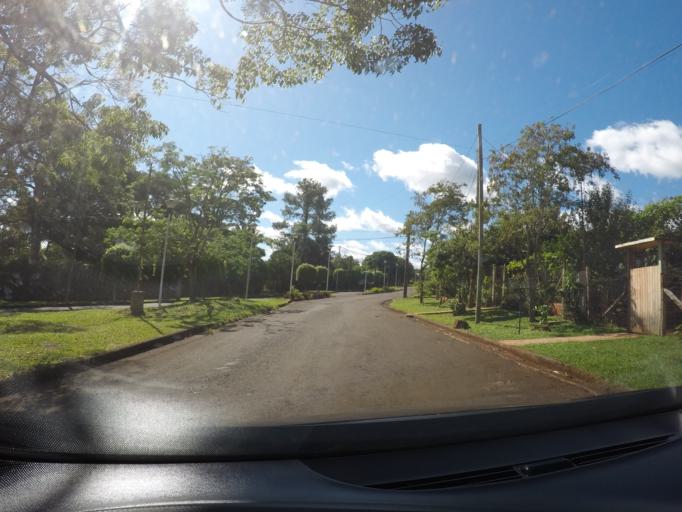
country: AR
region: Misiones
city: Puerto Rico
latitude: -26.7985
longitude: -55.0205
